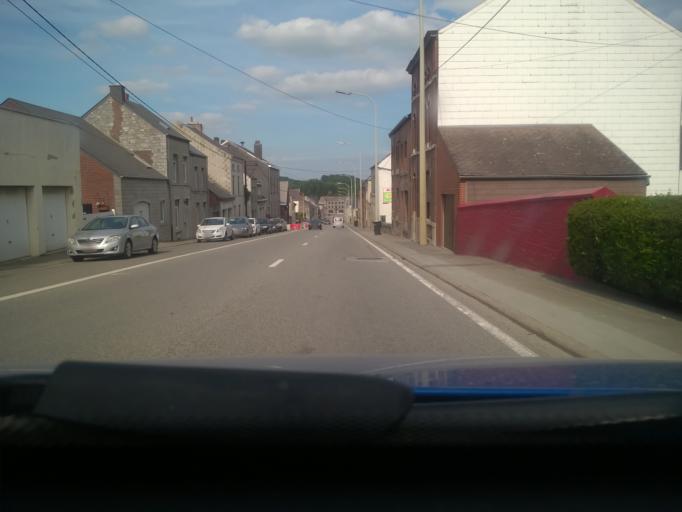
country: BE
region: Wallonia
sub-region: Province de Namur
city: Couvin
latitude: 50.0553
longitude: 4.4882
